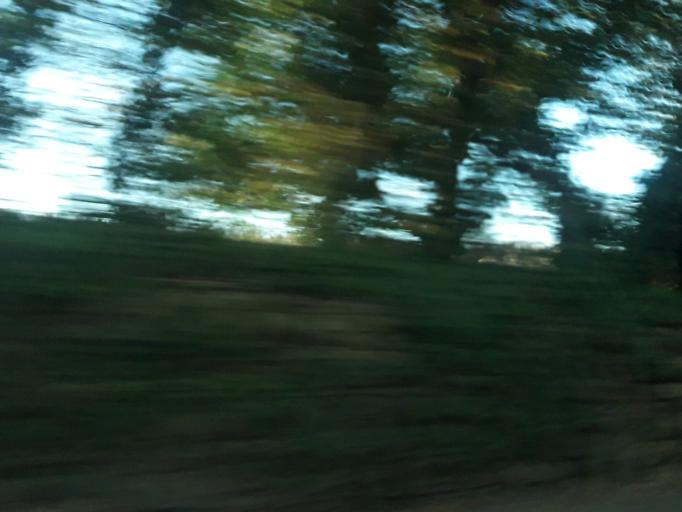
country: IE
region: Munster
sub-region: Ciarrai
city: Cill Airne
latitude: 52.0677
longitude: -9.5431
